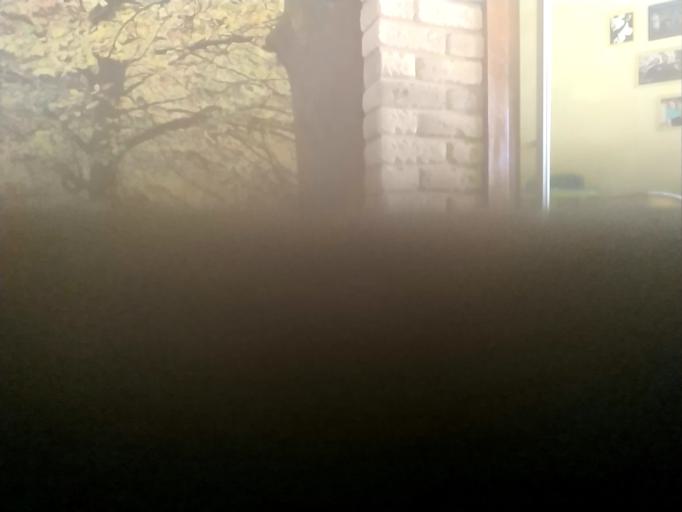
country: RU
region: Kaluga
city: Mosal'sk
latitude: 54.6496
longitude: 35.0707
